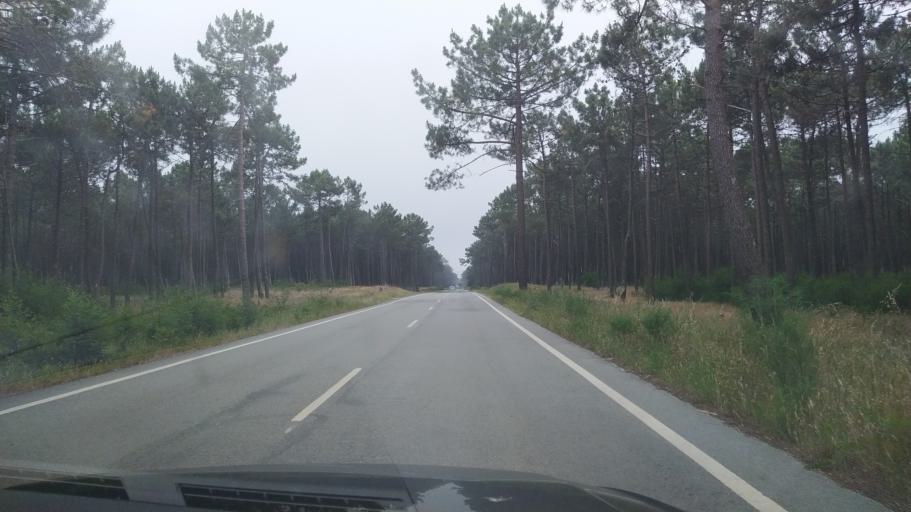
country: PT
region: Aveiro
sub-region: Ilhavo
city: Gafanha da Encarnacao
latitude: 40.5905
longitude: -8.7275
